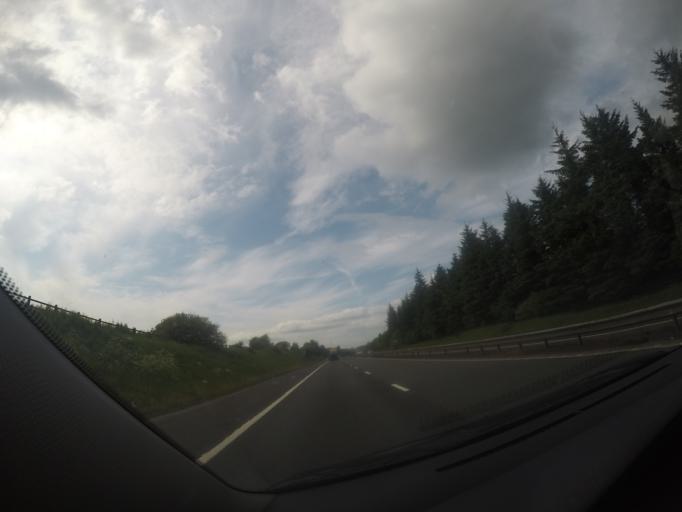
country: GB
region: Scotland
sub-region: South Lanarkshire
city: Douglas
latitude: 55.5881
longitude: -3.8289
